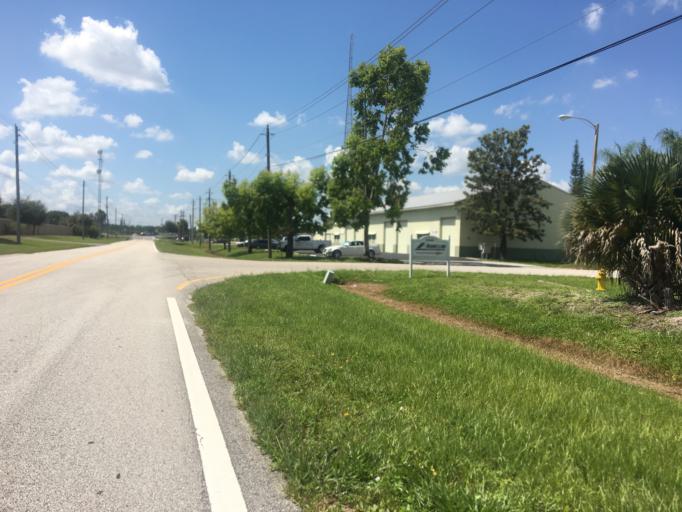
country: US
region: Florida
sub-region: Martin County
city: Palm City
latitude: 27.1642
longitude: -80.3023
